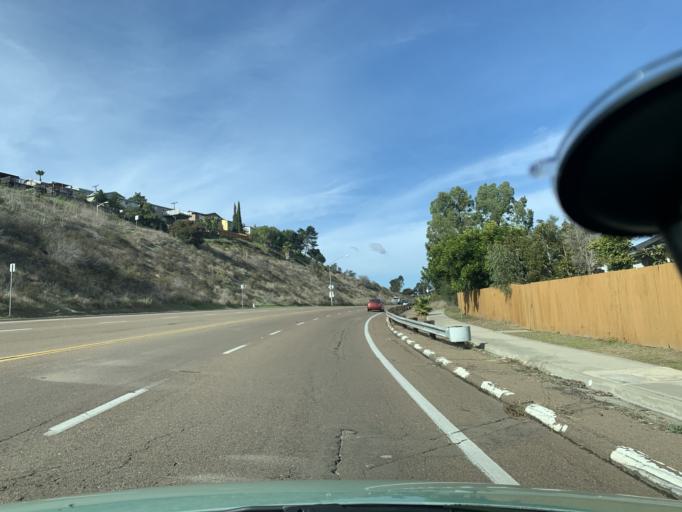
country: US
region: California
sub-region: San Diego County
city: San Diego
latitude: 32.8059
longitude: -117.1758
